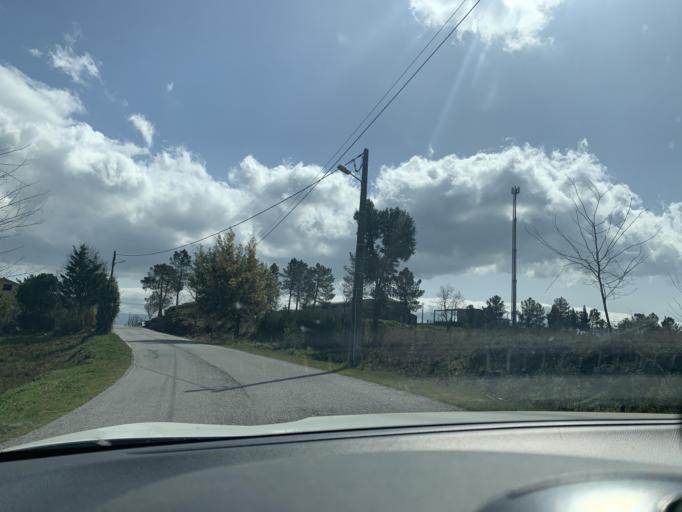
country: PT
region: Guarda
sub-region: Fornos de Algodres
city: Fornos de Algodres
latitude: 40.6139
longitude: -7.6090
